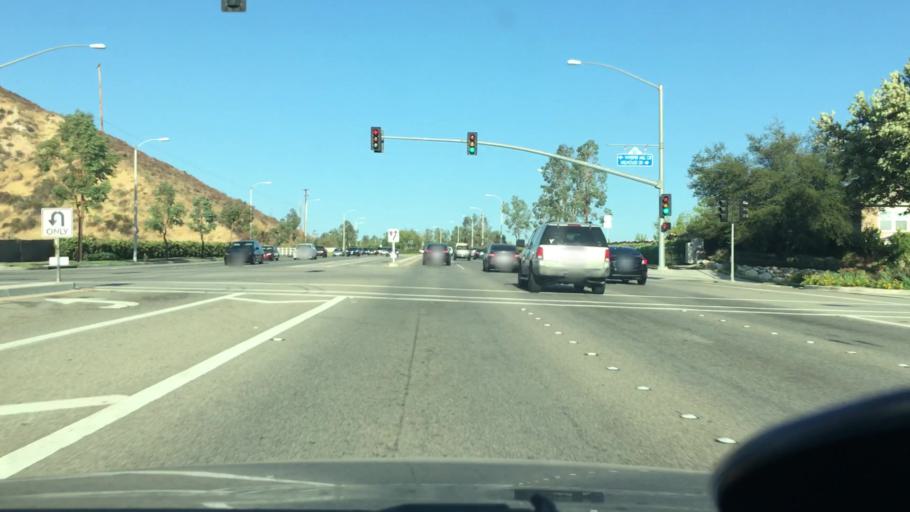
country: US
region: California
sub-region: Los Angeles County
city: Santa Clarita
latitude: 34.4250
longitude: -118.5295
